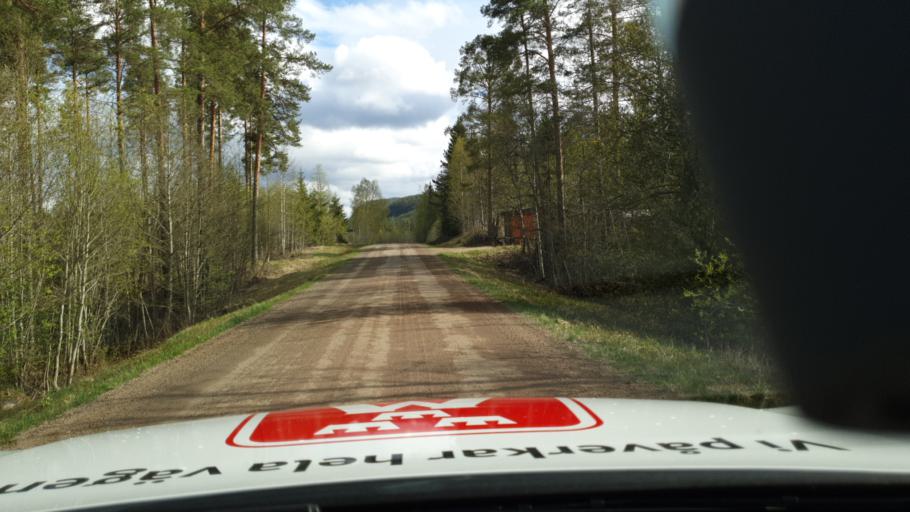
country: SE
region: Jaemtland
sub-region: Ragunda Kommun
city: Hammarstrand
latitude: 63.0885
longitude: 16.3334
